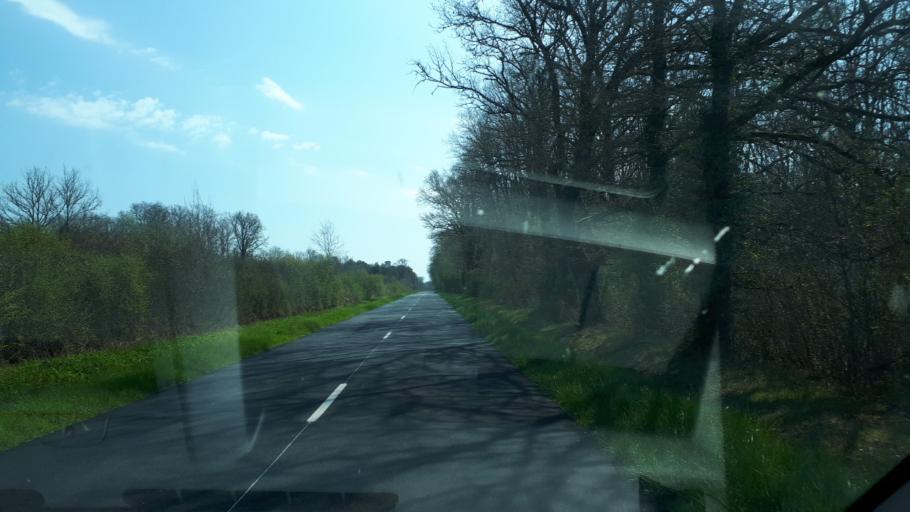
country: FR
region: Centre
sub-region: Departement du Loir-et-Cher
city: Selles-Saint-Denis
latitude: 47.3465
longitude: 1.8794
